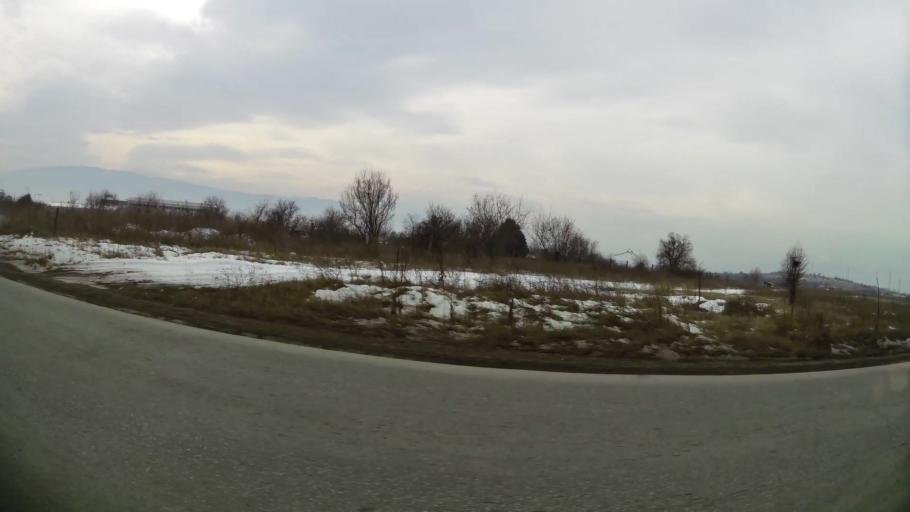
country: MK
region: Suto Orizari
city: Suto Orizare
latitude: 42.0447
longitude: 21.3887
